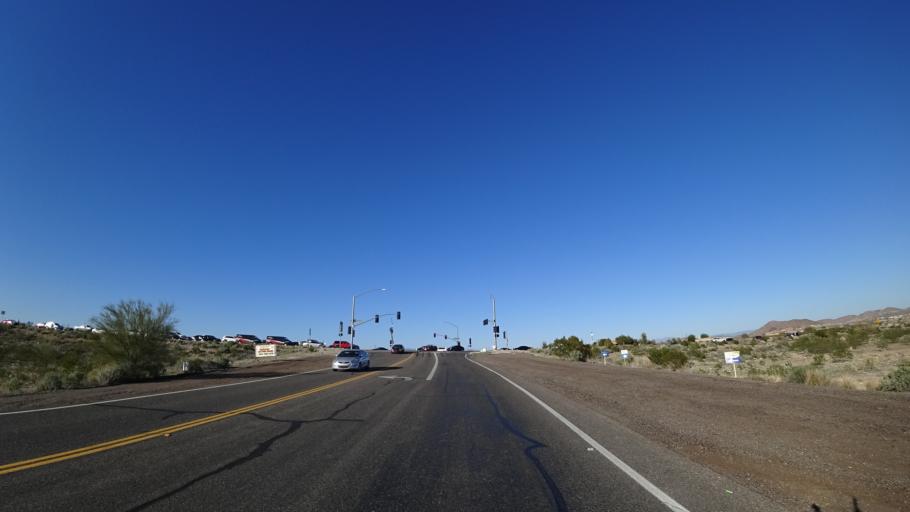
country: US
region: Arizona
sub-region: Maricopa County
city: Sun City West
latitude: 33.7128
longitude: -112.3063
